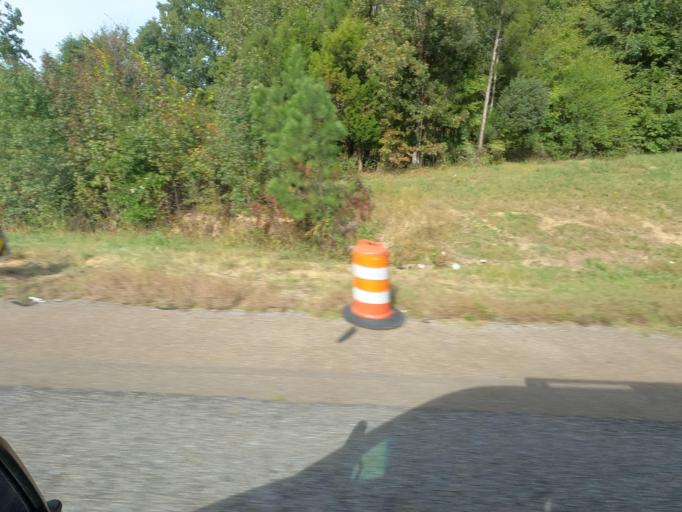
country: US
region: Tennessee
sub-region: Humphreys County
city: New Johnsonville
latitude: 35.8513
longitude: -88.0663
